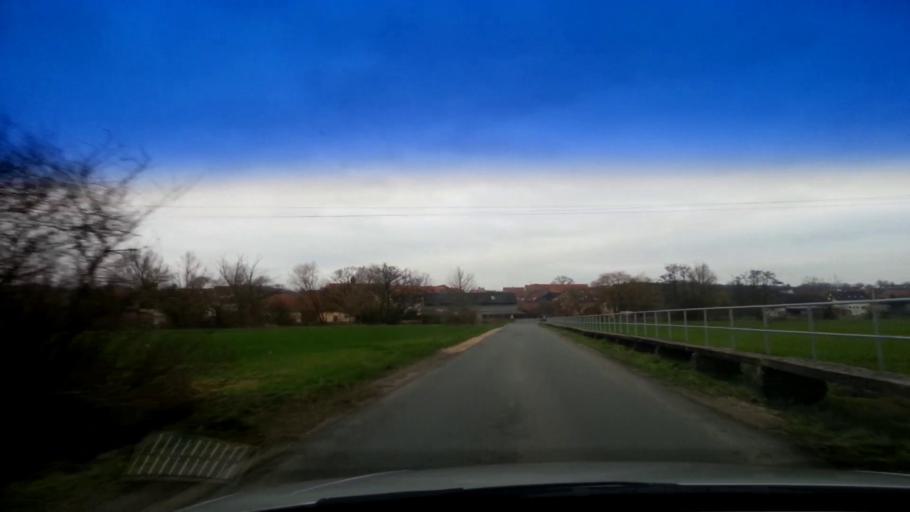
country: DE
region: Bavaria
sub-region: Upper Franconia
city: Walsdorf
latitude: 49.8213
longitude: 10.8076
